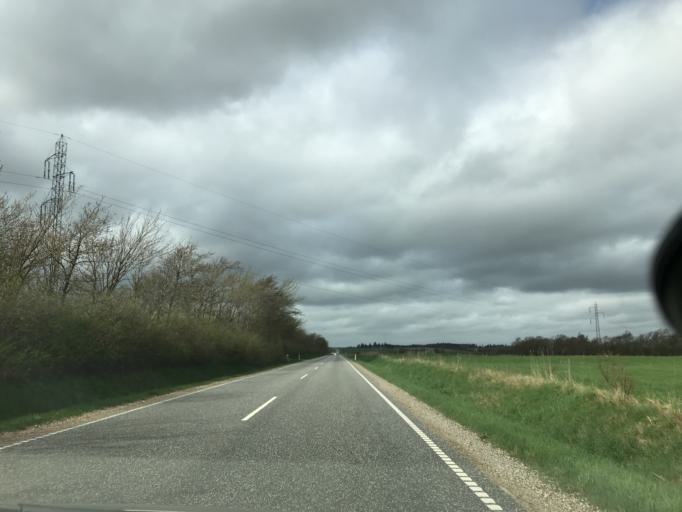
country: DK
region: Central Jutland
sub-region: Skive Kommune
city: Skive
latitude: 56.4929
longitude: 8.9564
